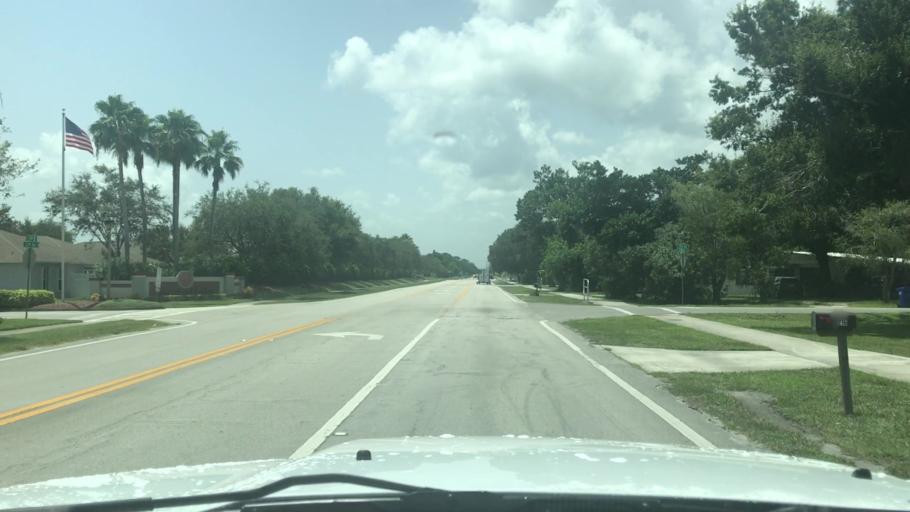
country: US
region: Florida
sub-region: Indian River County
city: Vero Beach
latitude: 27.6235
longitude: -80.3981
